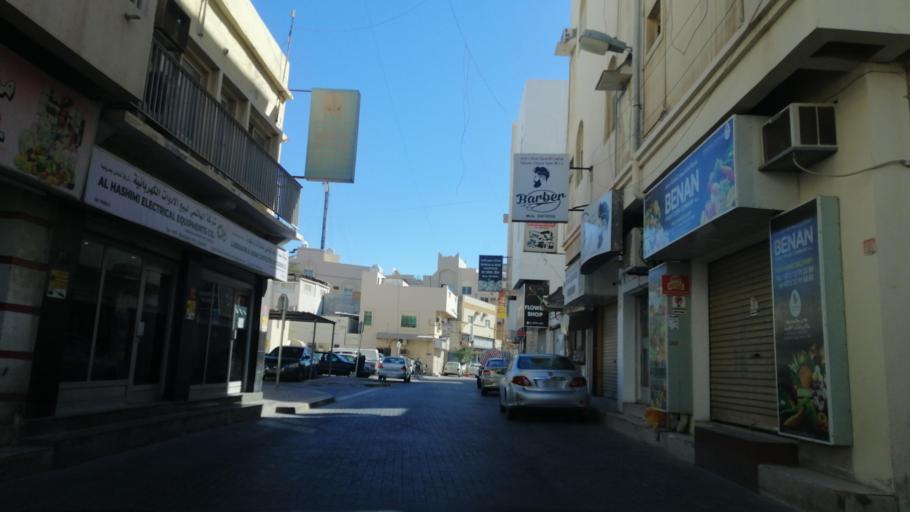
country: BH
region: Muharraq
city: Al Hadd
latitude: 26.2464
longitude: 50.6543
